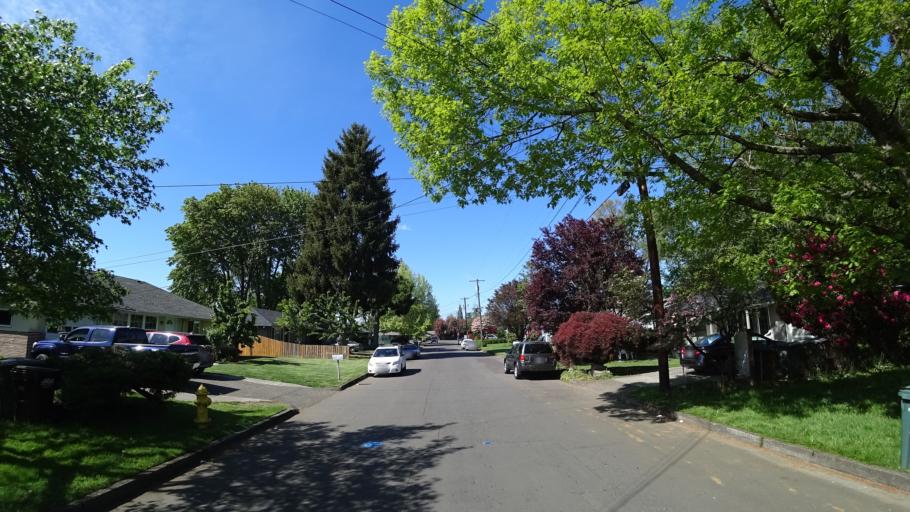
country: US
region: Oregon
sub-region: Washington County
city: Hillsboro
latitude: 45.5161
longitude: -122.9723
